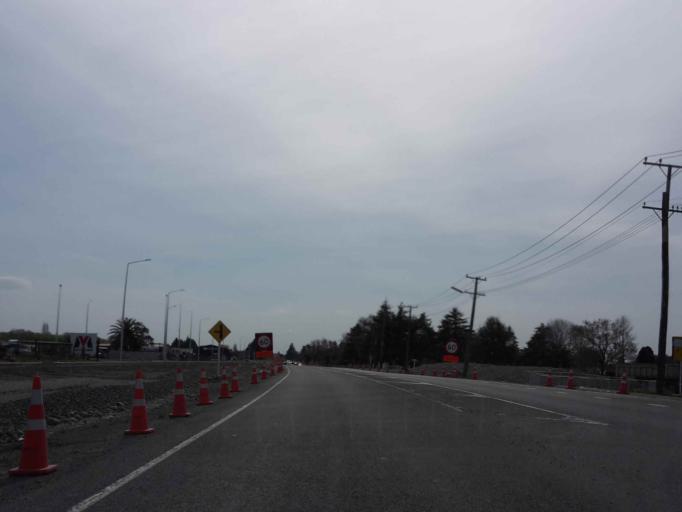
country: NZ
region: Canterbury
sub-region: Christchurch City
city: Christchurch
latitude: -43.4651
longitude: 172.5820
